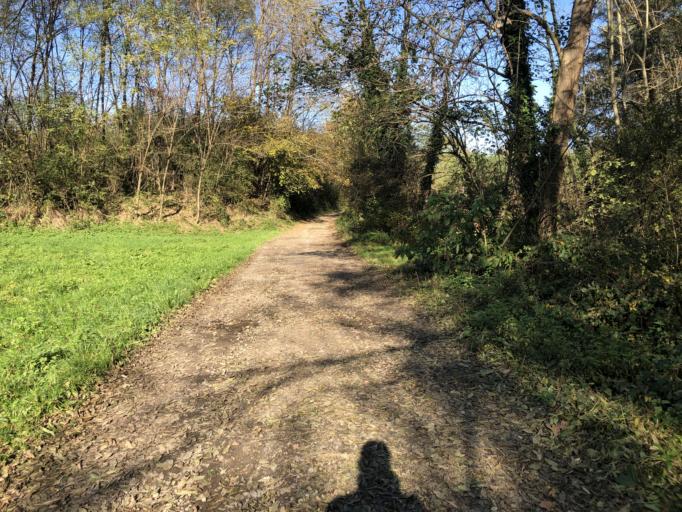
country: IT
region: Piedmont
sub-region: Provincia di Novara
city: Oleggio Castello
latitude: 45.7563
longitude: 8.5295
